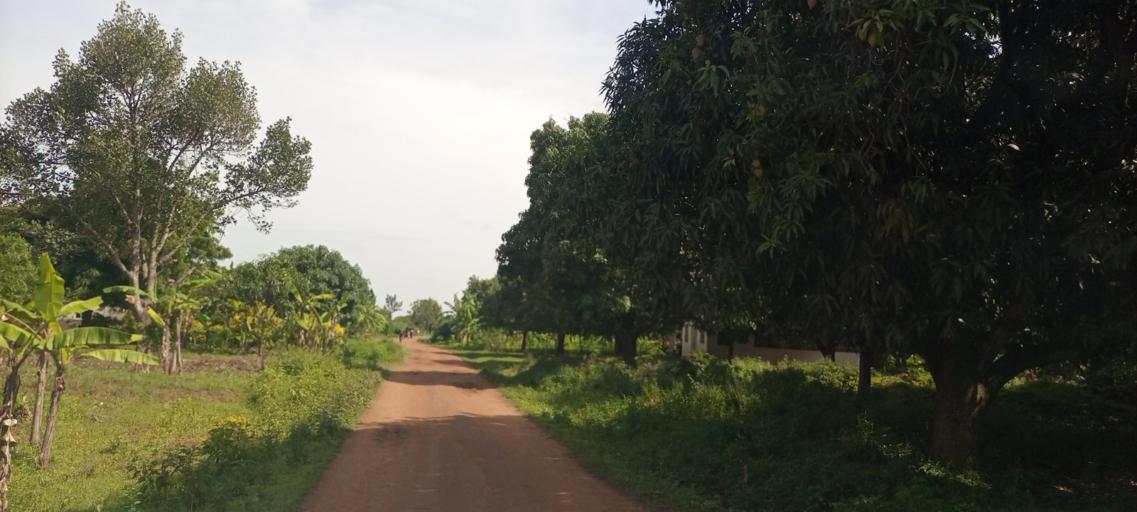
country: UG
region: Eastern Region
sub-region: Mbale District
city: Mbale
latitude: 1.1310
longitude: 34.0229
